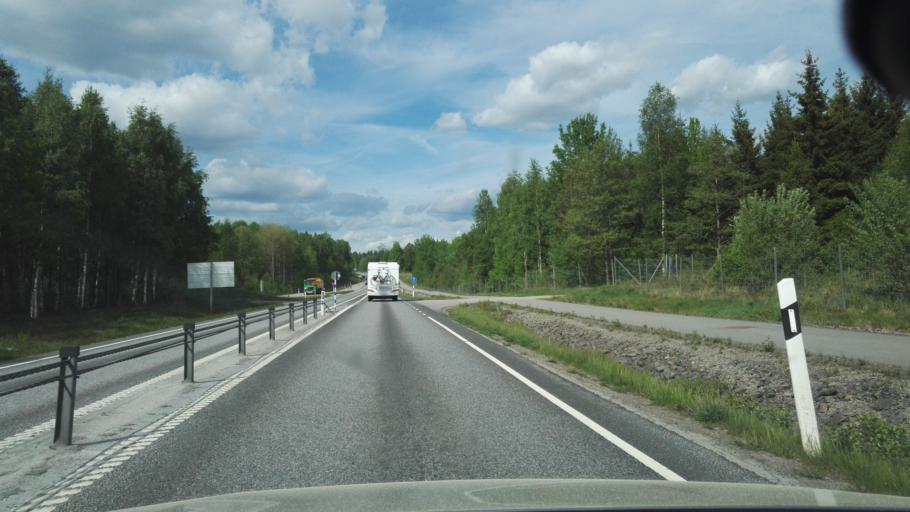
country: SE
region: Kronoberg
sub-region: Vaxjo Kommun
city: Vaexjoe
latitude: 56.9274
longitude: 14.8627
